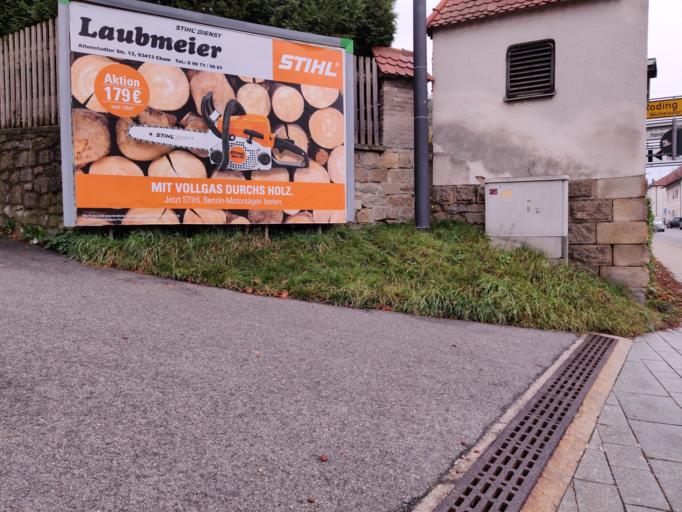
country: DE
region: Bavaria
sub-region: Upper Palatinate
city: Cham
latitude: 49.2223
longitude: 12.6603
